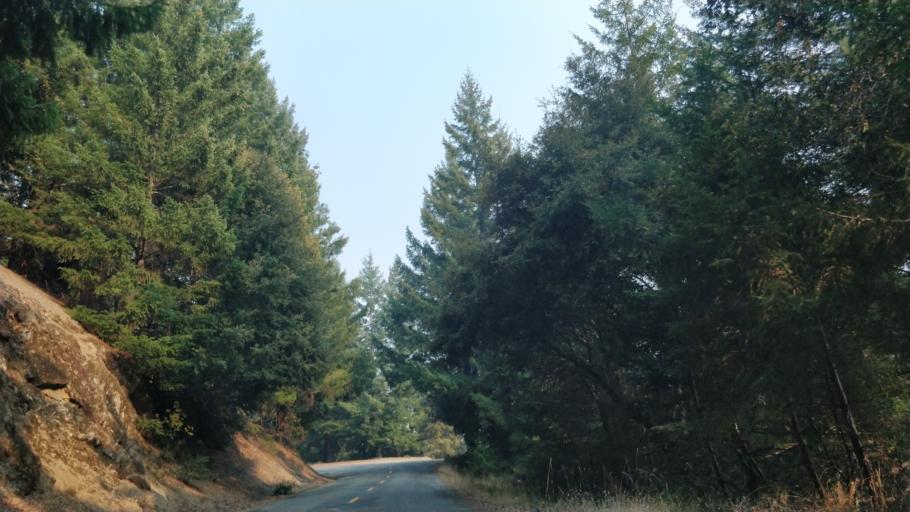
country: US
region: California
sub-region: Humboldt County
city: Rio Dell
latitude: 40.2678
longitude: -124.0786
